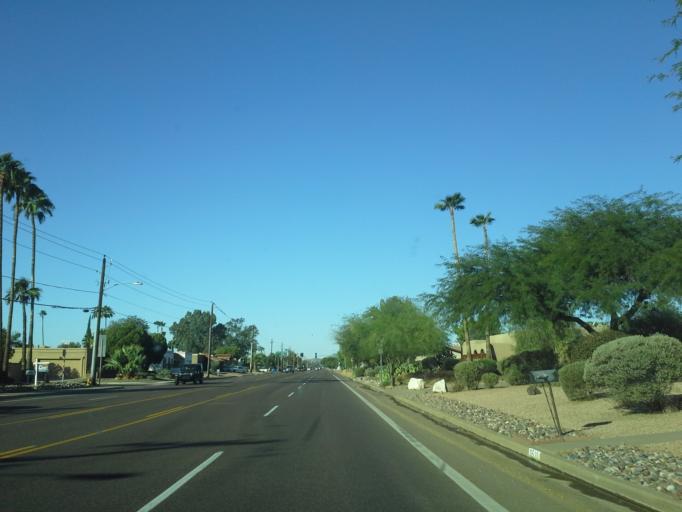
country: US
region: Arizona
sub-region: Maricopa County
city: Paradise Valley
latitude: 33.6114
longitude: -111.9402
